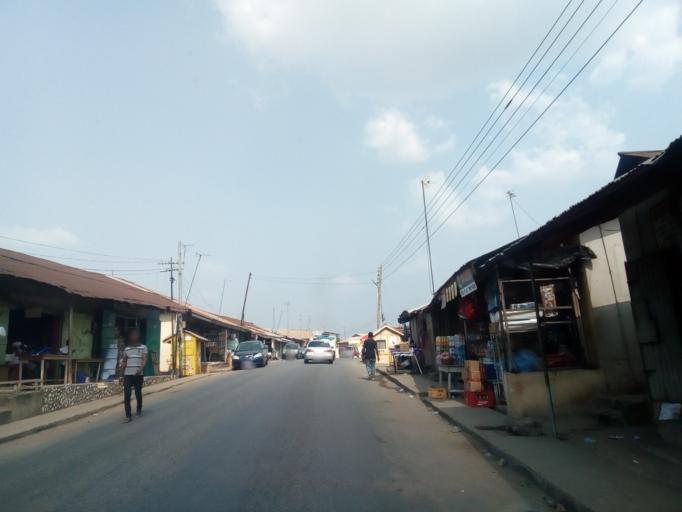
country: GH
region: Eastern
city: Suhum
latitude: 6.0409
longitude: -0.4481
